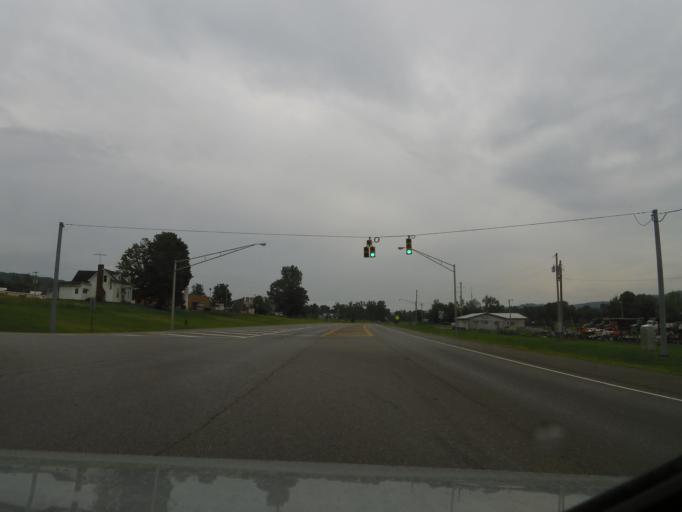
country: US
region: Ohio
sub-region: Brown County
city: Aberdeen
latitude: 38.6842
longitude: -83.7755
